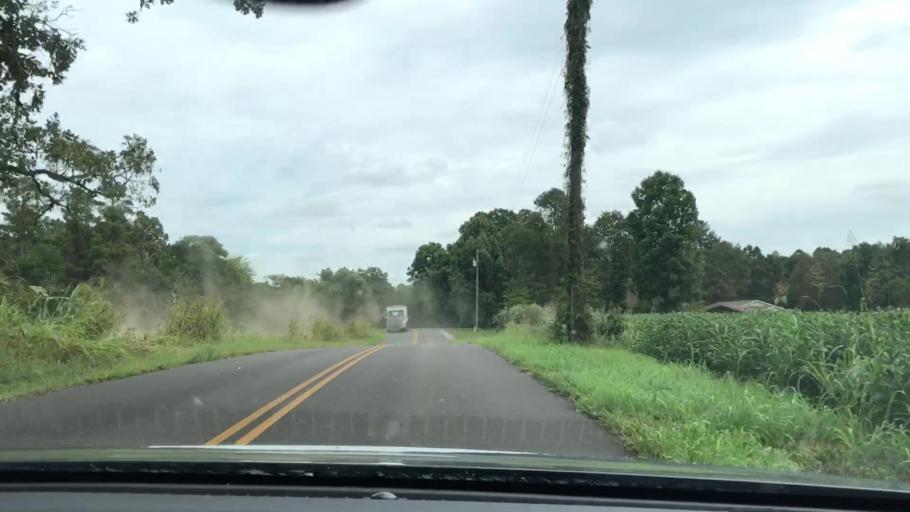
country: US
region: Kentucky
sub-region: Marshall County
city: Benton
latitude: 36.8317
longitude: -88.3635
